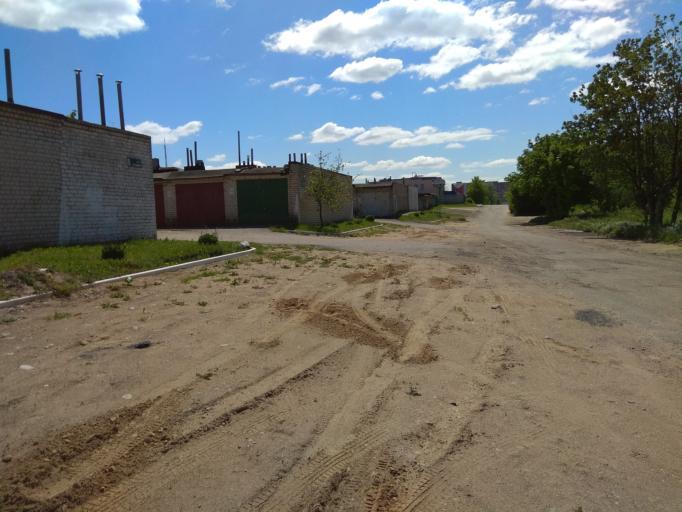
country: BY
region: Grodnenskaya
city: Hrodna
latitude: 53.7128
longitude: 23.8015
